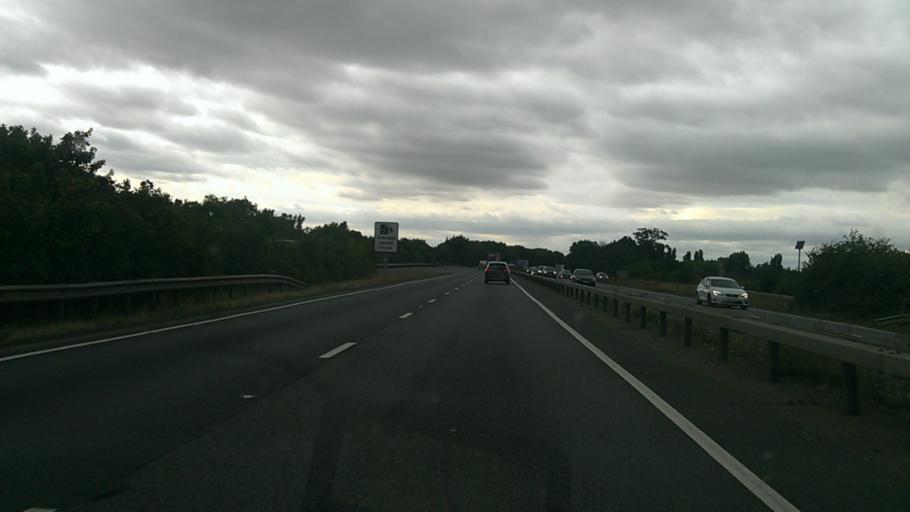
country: GB
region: England
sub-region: Cambridgeshire
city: Godmanchester
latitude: 52.3189
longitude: -0.1604
